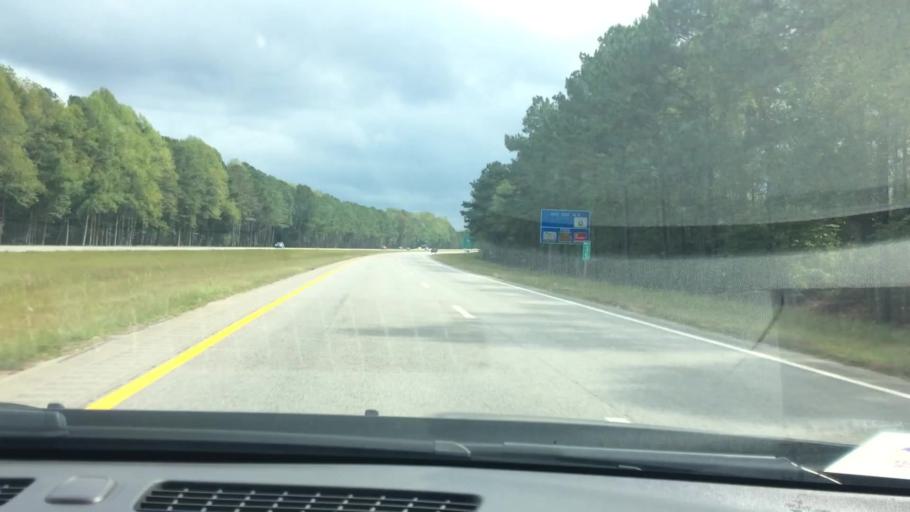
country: US
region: North Carolina
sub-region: Wilson County
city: Lucama
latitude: 35.7705
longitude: -78.0423
